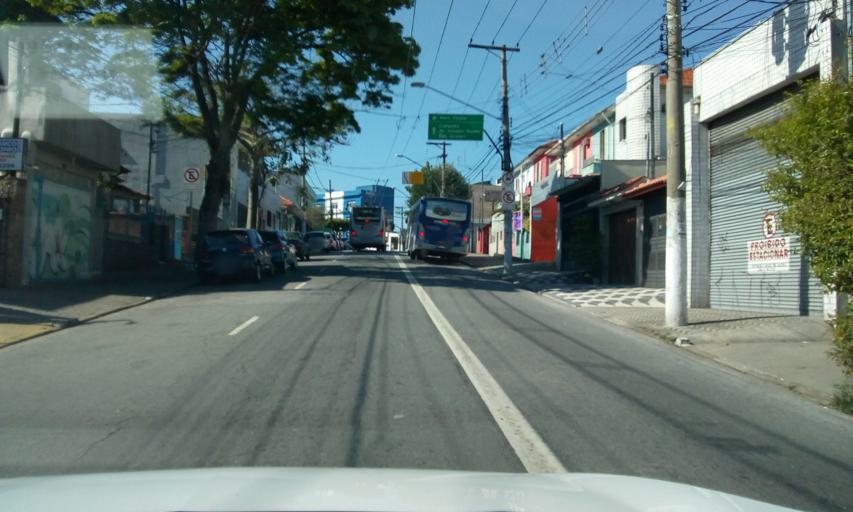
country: BR
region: Sao Paulo
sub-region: Guarulhos
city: Guarulhos
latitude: -23.5203
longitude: -46.5475
